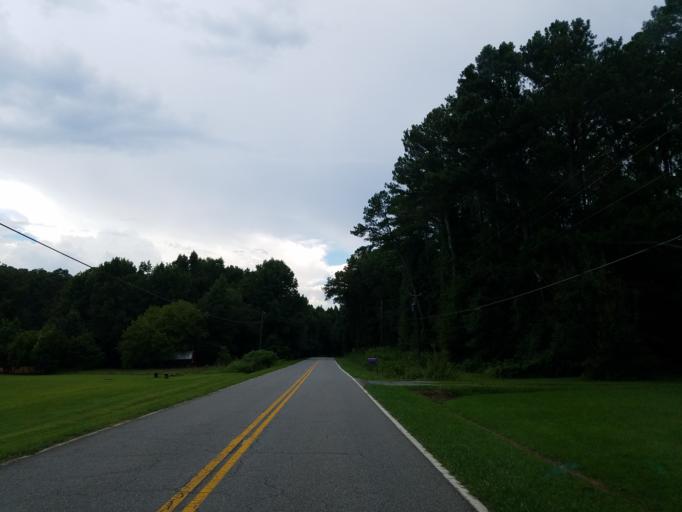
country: US
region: Georgia
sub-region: Bartow County
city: Cartersville
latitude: 34.2558
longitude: -84.8562
